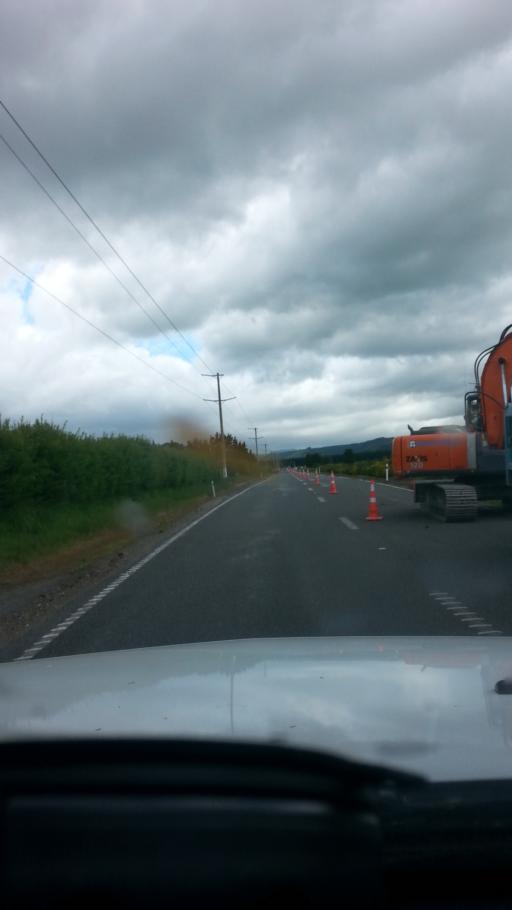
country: NZ
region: Wellington
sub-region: Masterton District
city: Masterton
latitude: -40.8246
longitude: 175.6249
